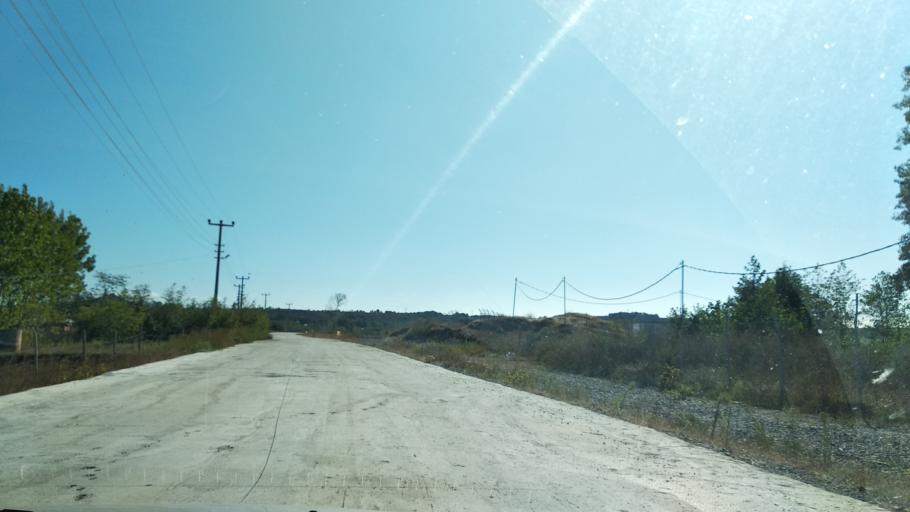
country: TR
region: Sakarya
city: Karasu
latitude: 41.1253
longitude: 30.6086
